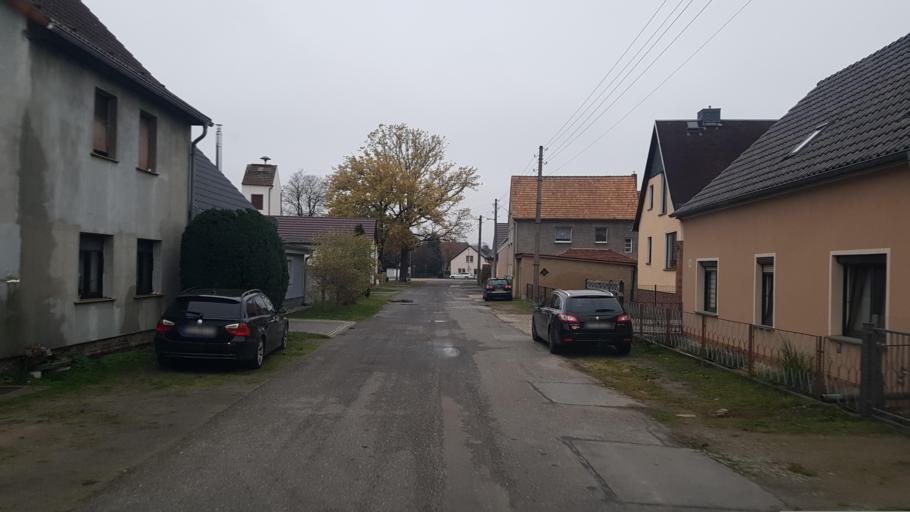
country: DE
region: Brandenburg
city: Ruhland
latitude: 51.4285
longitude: 13.8584
